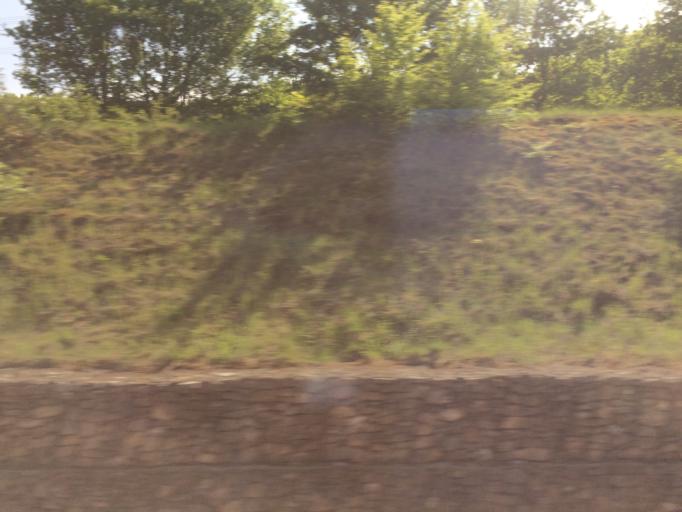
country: DE
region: Bavaria
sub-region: Regierungsbezirk Mittelfranken
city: Langenfeld
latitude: 49.6267
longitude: 10.4975
